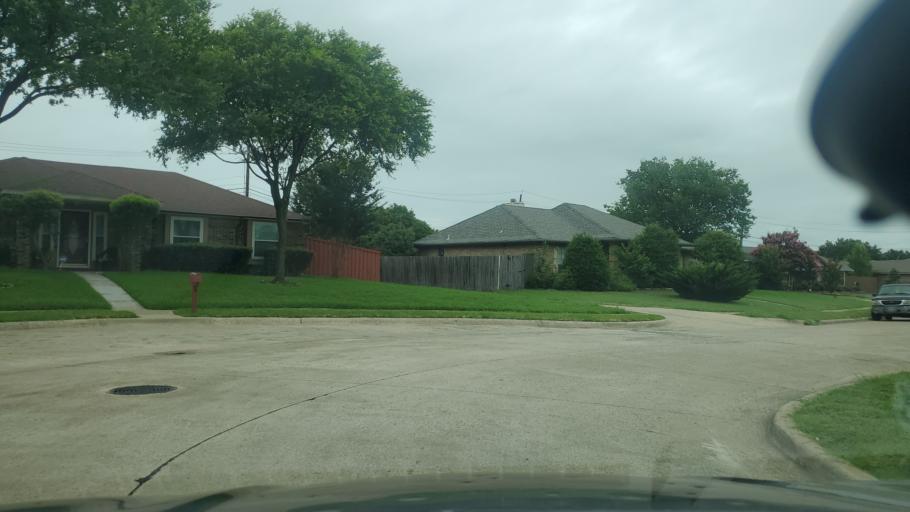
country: US
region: Texas
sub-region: Dallas County
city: Garland
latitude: 32.9393
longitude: -96.6347
